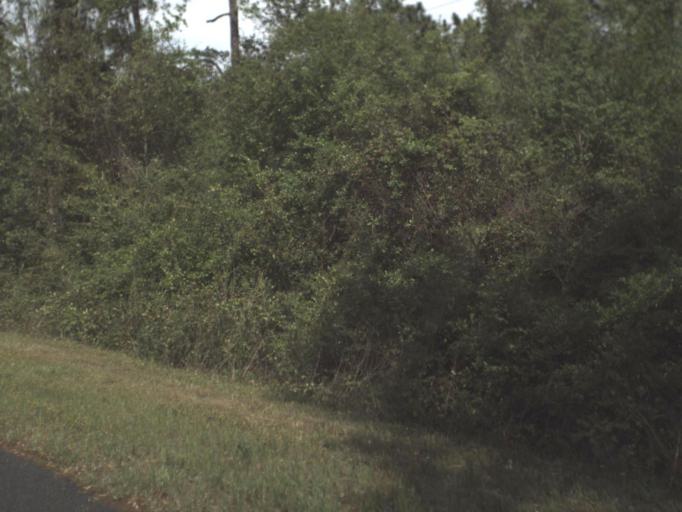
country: US
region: Florida
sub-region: Santa Rosa County
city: Pace
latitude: 30.5868
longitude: -87.1772
